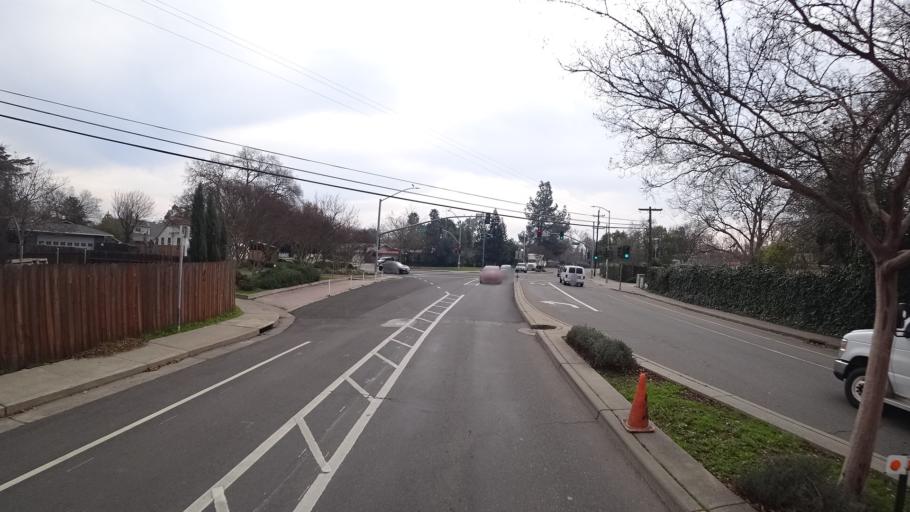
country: US
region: California
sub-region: Yolo County
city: Davis
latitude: 38.5579
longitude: -121.7279
